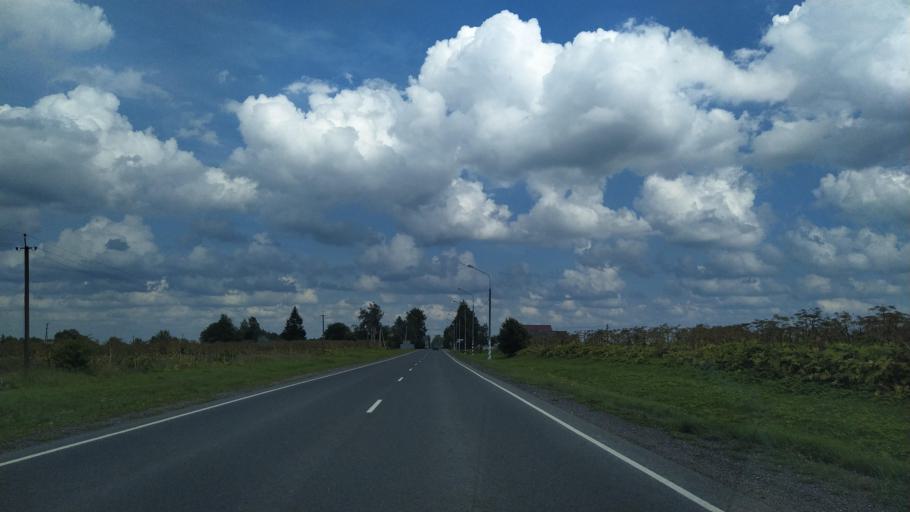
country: RU
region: Novgorod
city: Sol'tsy
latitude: 58.0811
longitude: 30.0908
